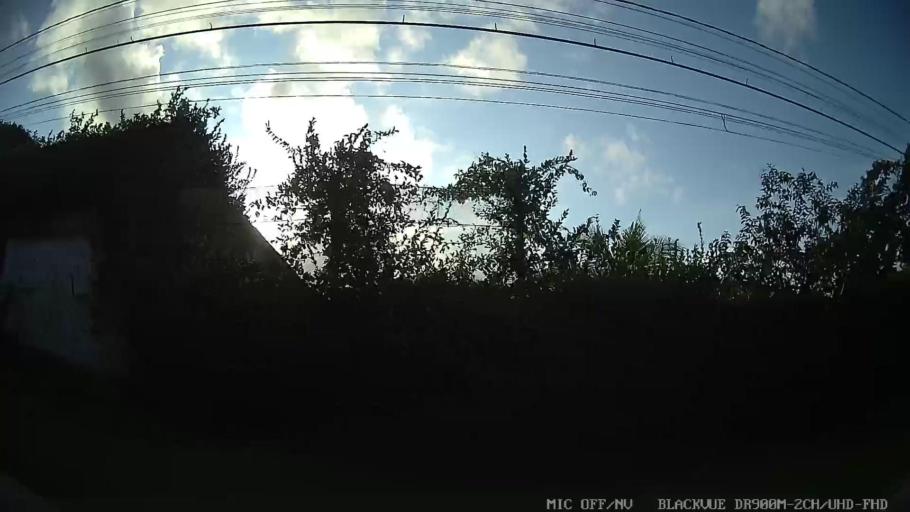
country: BR
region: Sao Paulo
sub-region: Itanhaem
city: Itanhaem
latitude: -24.1509
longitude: -46.8205
